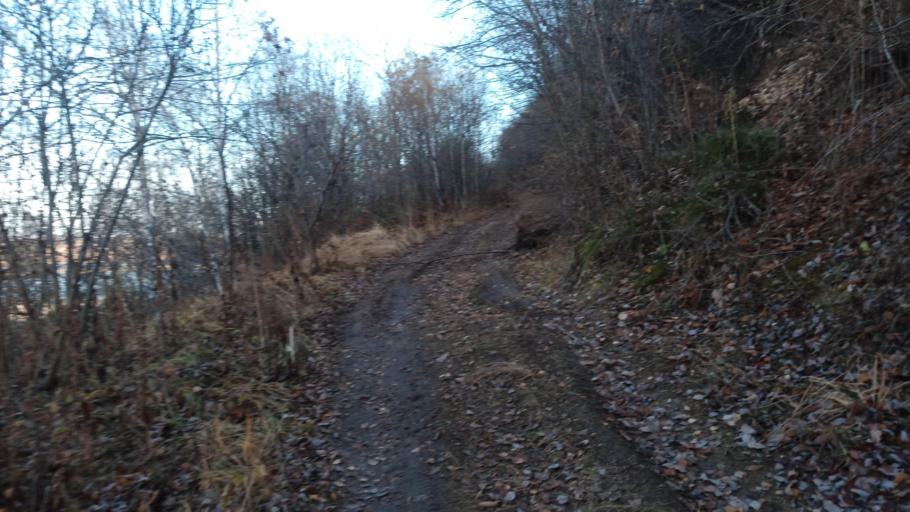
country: RU
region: Altai Krai
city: Gon'ba
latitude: 53.4344
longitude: 83.5504
